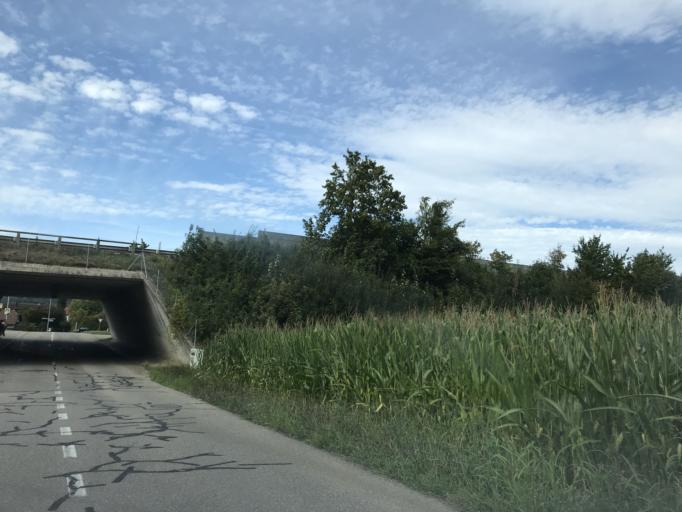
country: CH
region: Aargau
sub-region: Bezirk Rheinfelden
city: Stein
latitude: 47.5403
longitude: 7.9553
